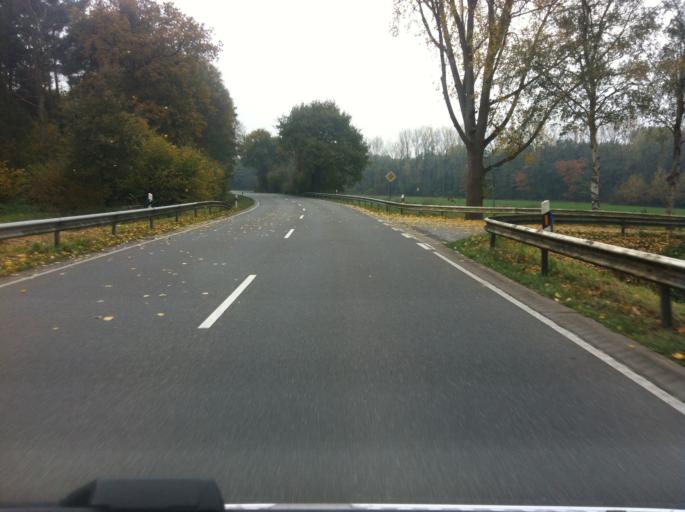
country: DE
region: North Rhine-Westphalia
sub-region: Regierungsbezirk Munster
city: Sudlohn
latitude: 51.9782
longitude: 6.8376
